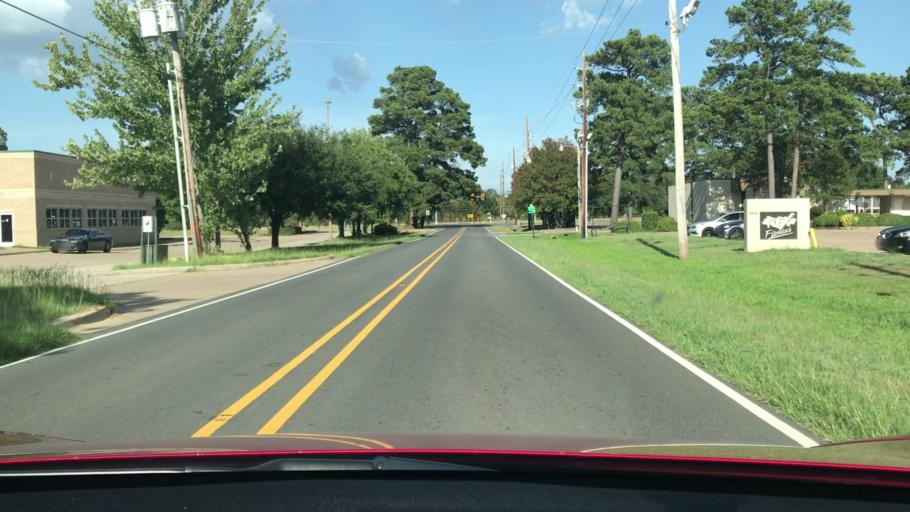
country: US
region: Louisiana
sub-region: Bossier Parish
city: Bossier City
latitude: 32.4204
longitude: -93.7897
